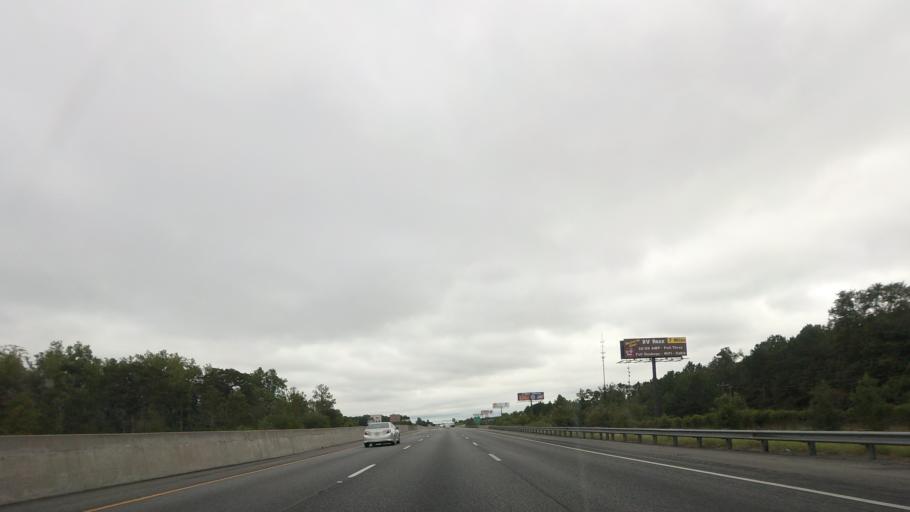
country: US
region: Georgia
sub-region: Lowndes County
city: Hahira
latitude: 31.0013
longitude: -83.3910
